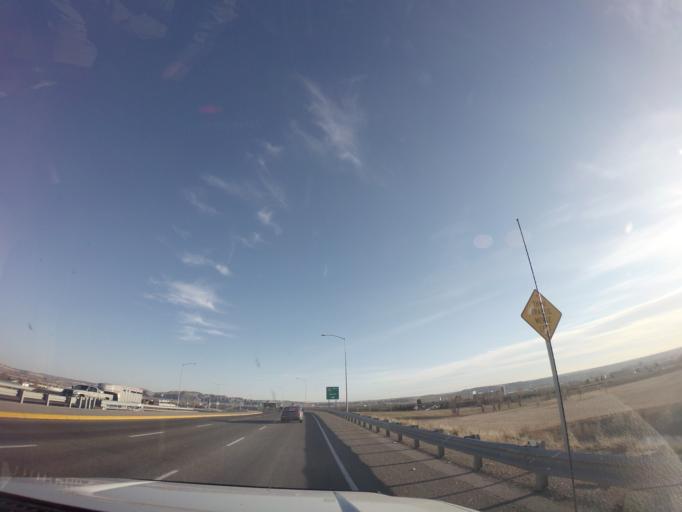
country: US
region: Montana
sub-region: Yellowstone County
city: Billings
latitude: 45.7522
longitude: -108.5614
